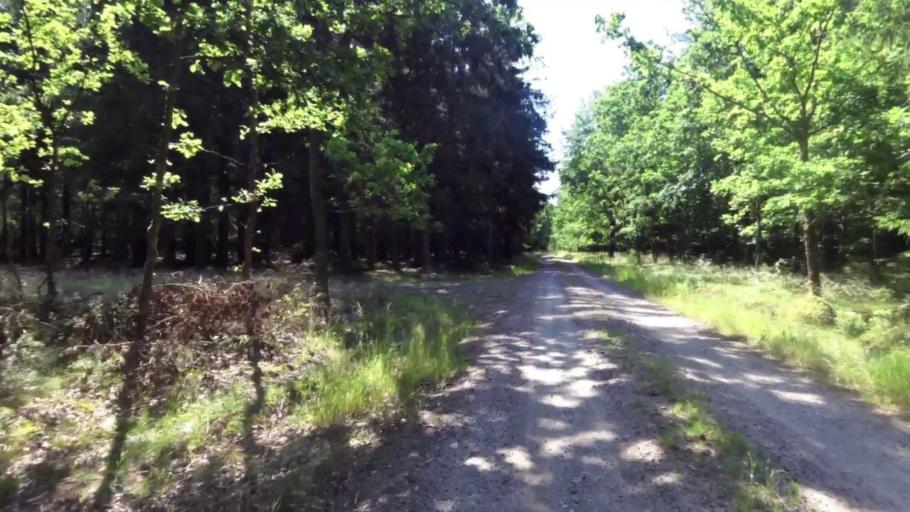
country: PL
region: West Pomeranian Voivodeship
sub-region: Powiat swidwinski
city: Polczyn-Zdroj
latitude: 53.8462
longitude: 16.1449
